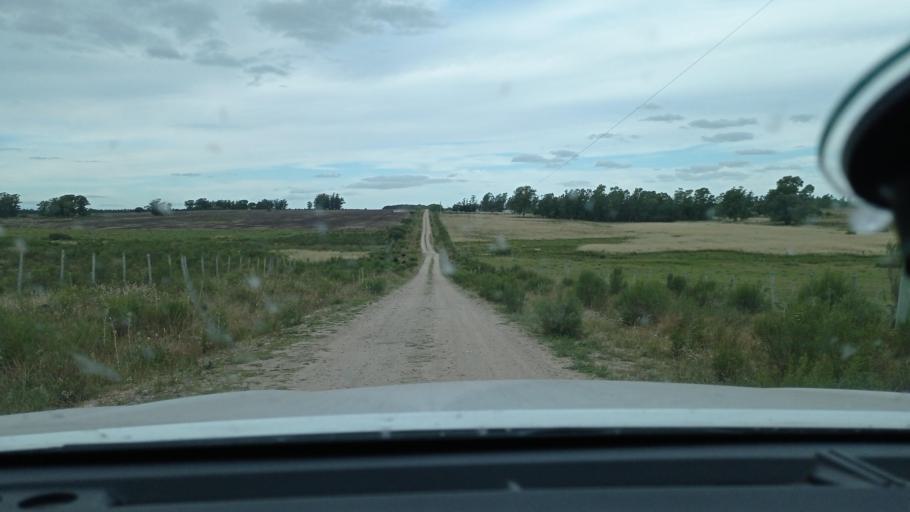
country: UY
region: Florida
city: Casupa
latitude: -34.1171
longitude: -55.8284
